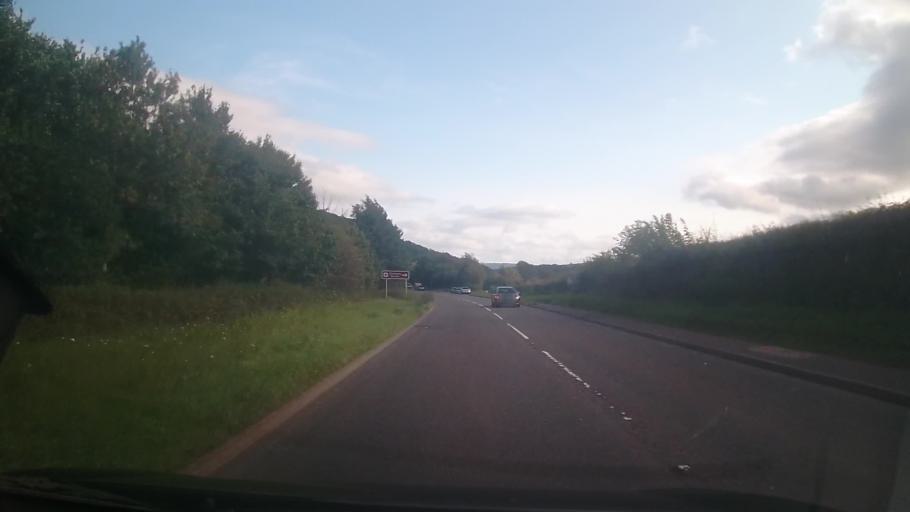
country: GB
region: England
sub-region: Shropshire
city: Craven Arms
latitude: 52.4341
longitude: -2.8302
